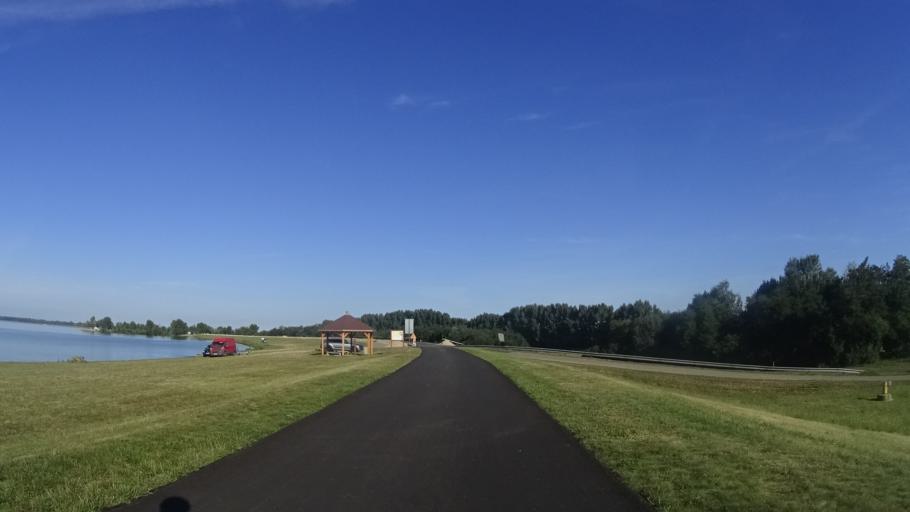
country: SK
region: Trnavsky
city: Samorin
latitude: 48.0198
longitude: 17.2888
